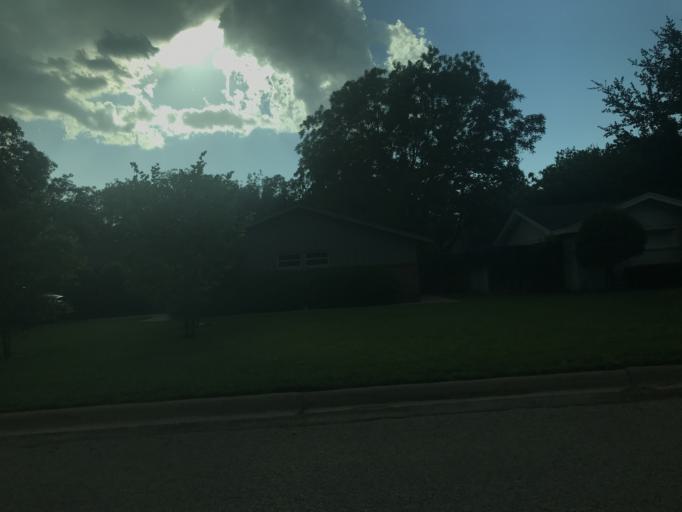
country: US
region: Texas
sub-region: Taylor County
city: Abilene
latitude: 32.4272
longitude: -99.7696
